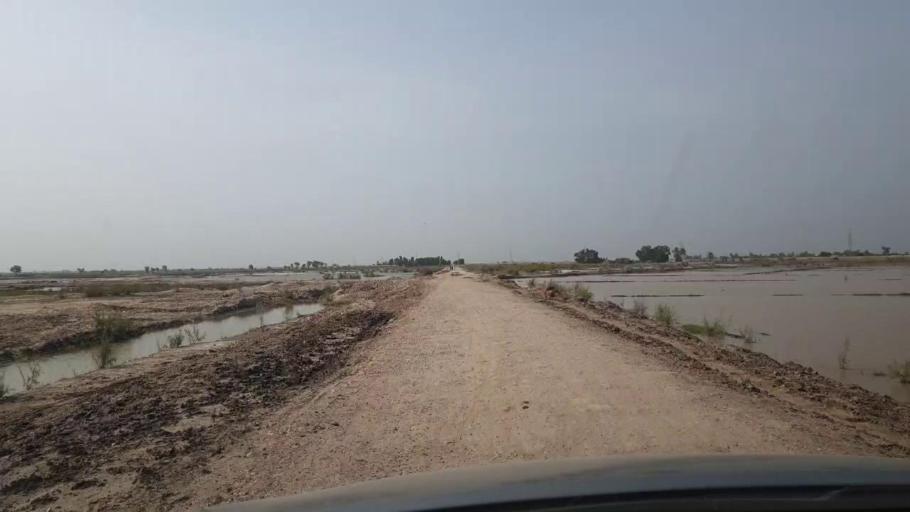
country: PK
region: Sindh
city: Lakhi
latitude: 27.8399
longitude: 68.6997
